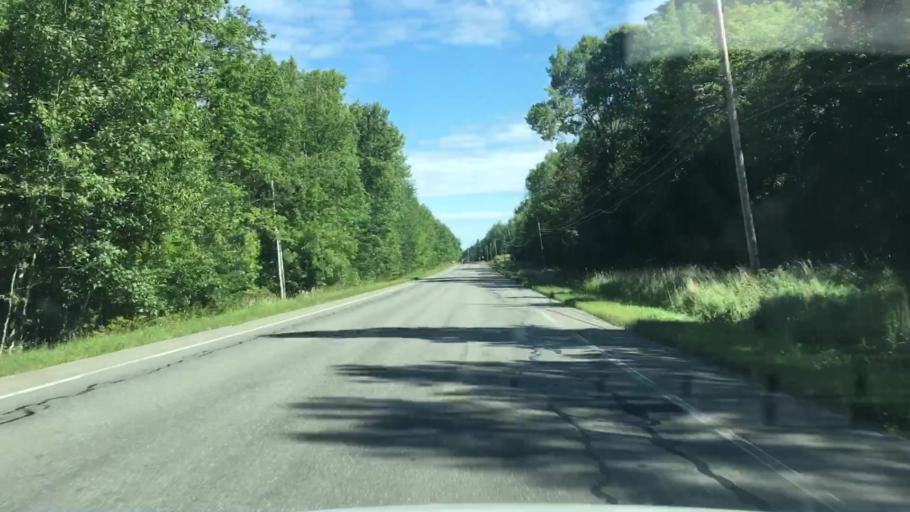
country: US
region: Maine
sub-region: Penobscot County
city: Dexter
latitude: 45.0636
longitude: -69.2460
